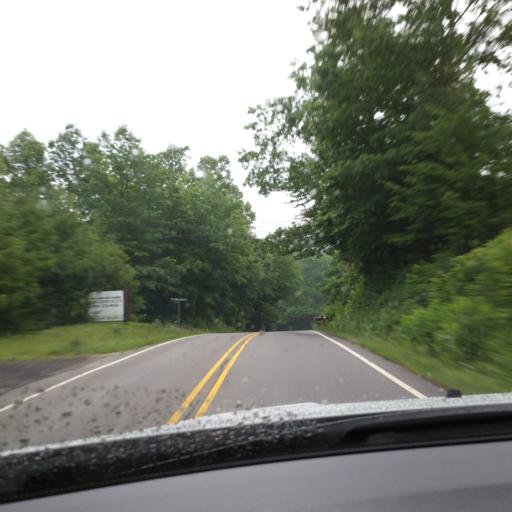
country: US
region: North Carolina
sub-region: Yancey County
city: Burnsville
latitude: 35.7705
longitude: -82.1871
